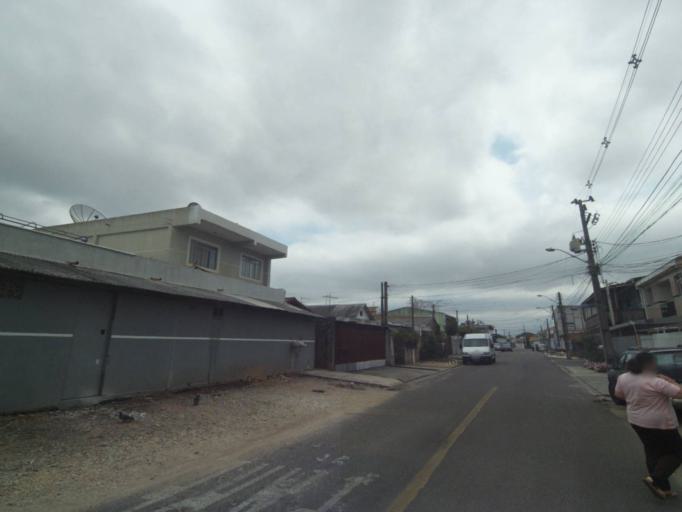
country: BR
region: Parana
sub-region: Sao Jose Dos Pinhais
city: Sao Jose dos Pinhais
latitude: -25.5440
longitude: -49.2529
